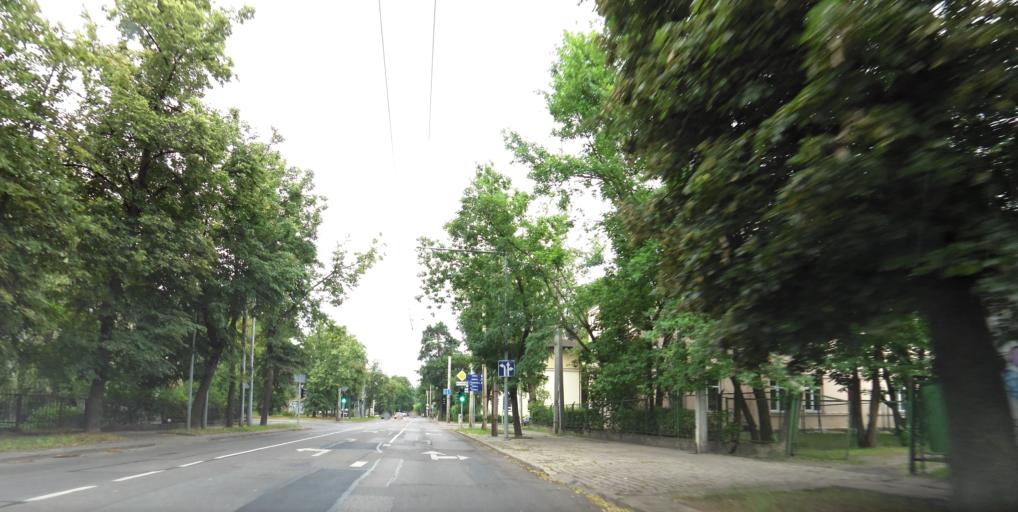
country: LT
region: Vilnius County
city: Seskine
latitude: 54.6905
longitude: 25.2516
